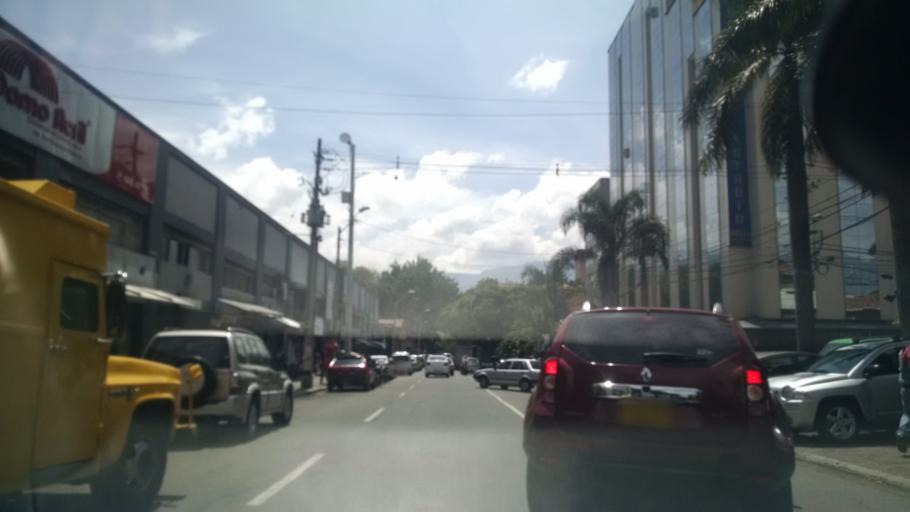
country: CO
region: Antioquia
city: Medellin
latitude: 6.2577
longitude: -75.5857
